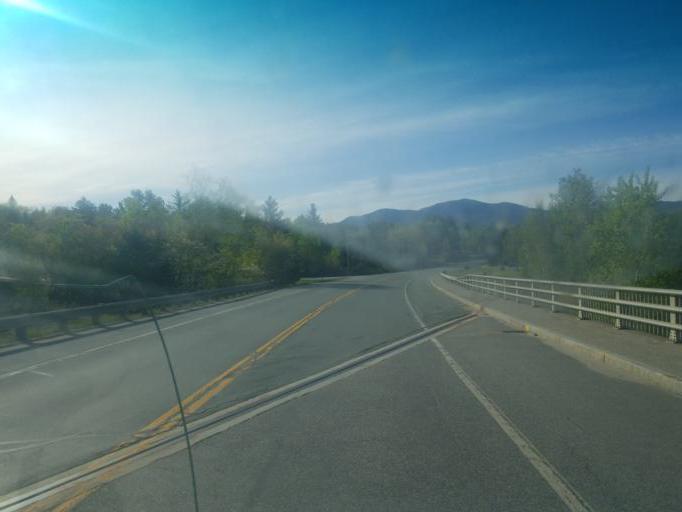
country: US
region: New Hampshire
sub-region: Grafton County
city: Deerfield
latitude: 44.2726
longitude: -71.6320
